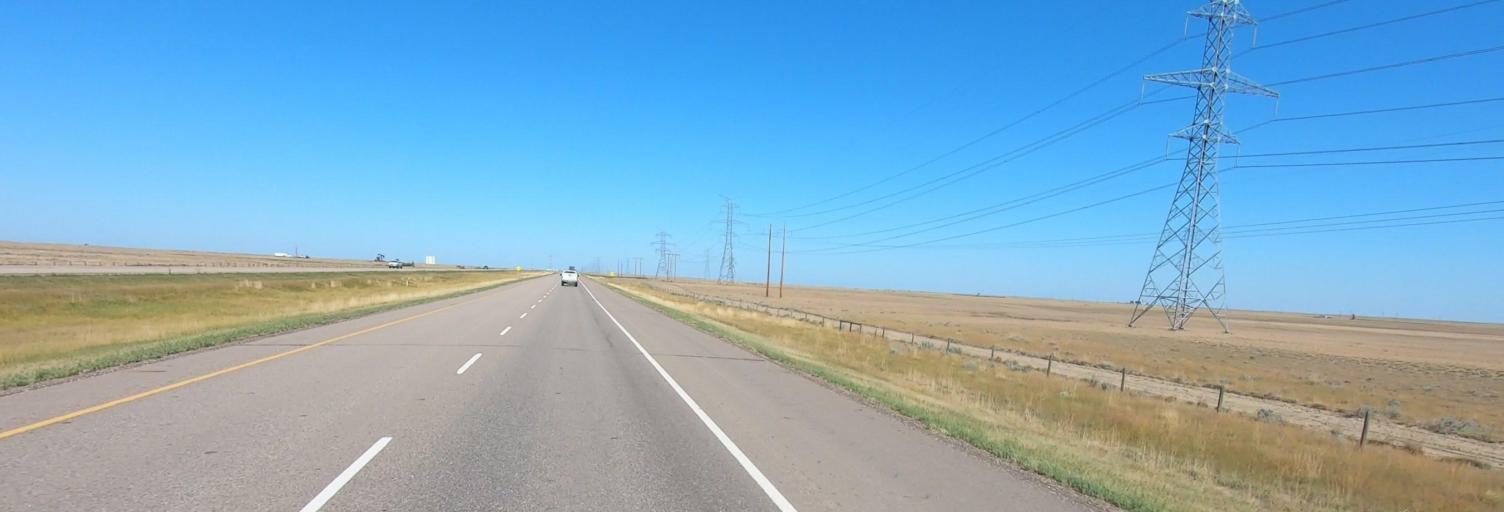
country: CA
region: Alberta
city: Brooks
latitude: 50.4146
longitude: -111.5114
